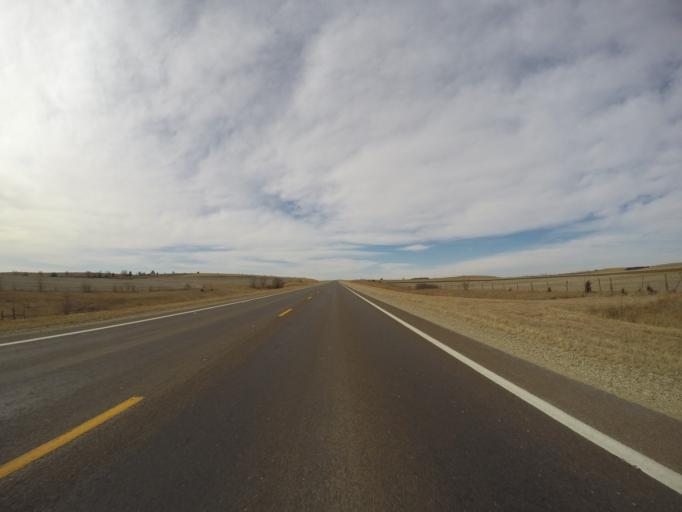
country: US
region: Kansas
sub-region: Washington County
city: Washington
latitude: 39.8171
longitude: -96.9293
